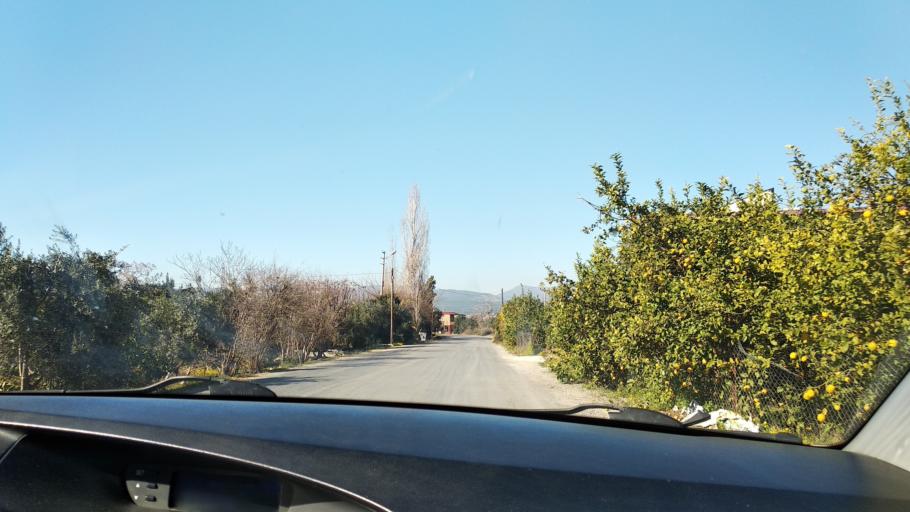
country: TR
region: Mersin
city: Tomuk
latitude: 36.6619
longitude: 34.3645
